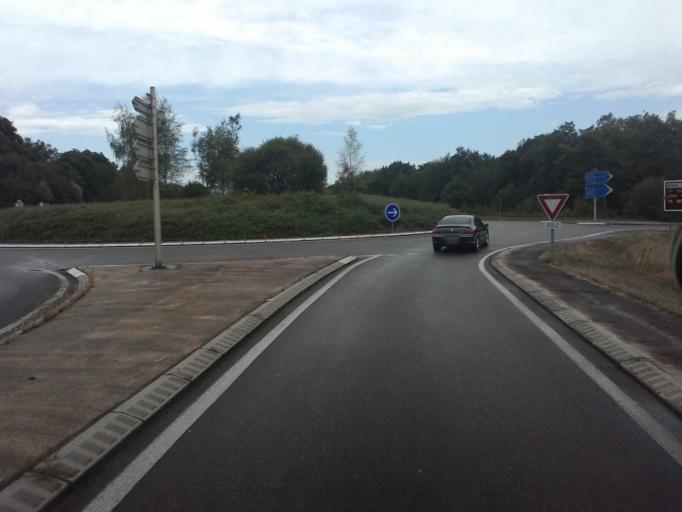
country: FR
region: Franche-Comte
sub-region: Departement du Jura
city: Poligny
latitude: 46.8417
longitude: 5.6216
